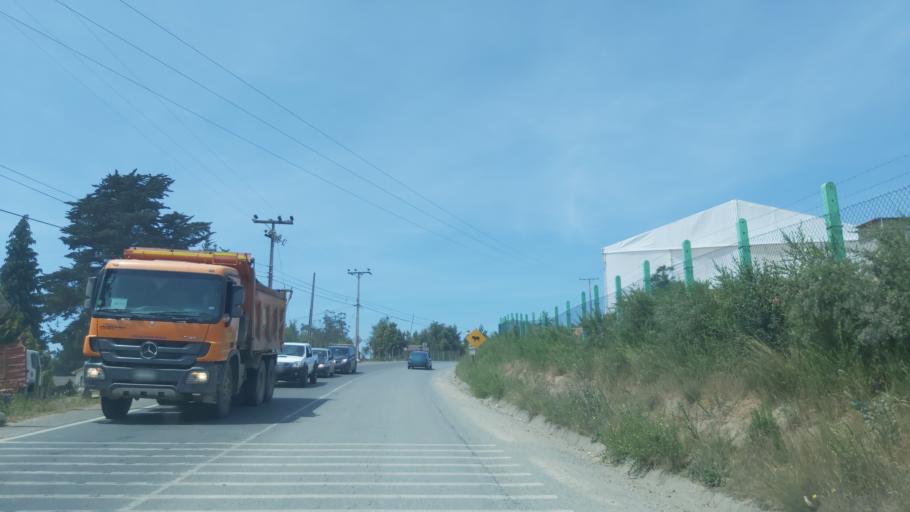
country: CL
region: Maule
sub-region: Provincia de Talca
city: Constitucion
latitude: -35.3753
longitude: -72.4199
